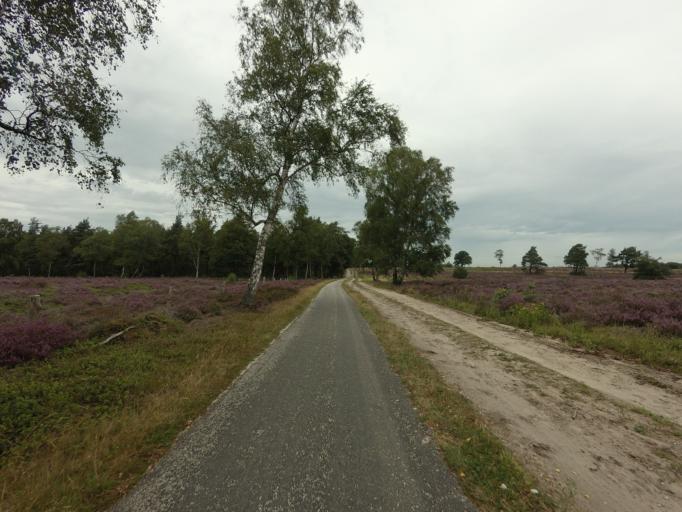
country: NL
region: Overijssel
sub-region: Gemeente Raalte
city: Raalte
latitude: 52.3466
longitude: 6.4031
